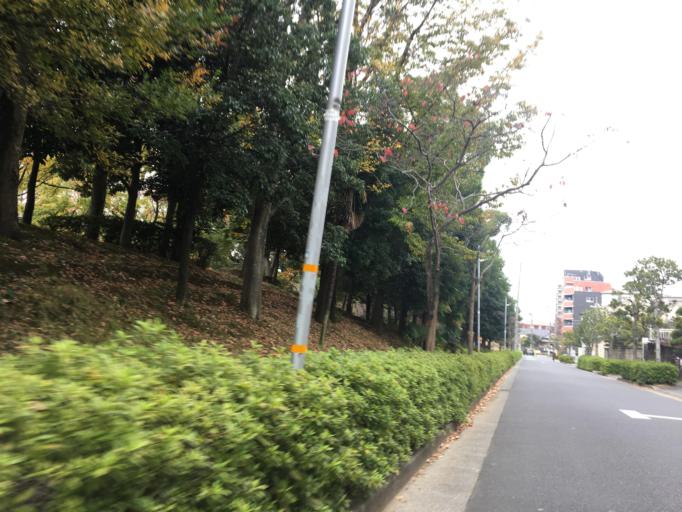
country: JP
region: Tokyo
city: Urayasu
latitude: 35.6496
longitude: 139.8776
